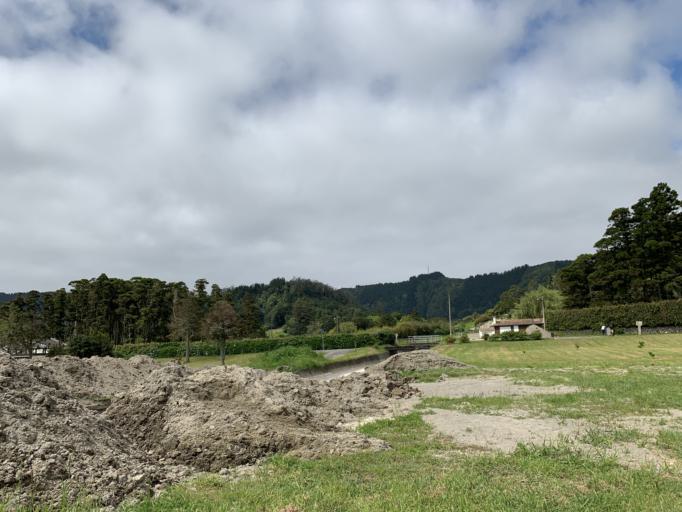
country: PT
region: Azores
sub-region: Ponta Delgada
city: Arrifes
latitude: 37.8664
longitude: -25.7935
